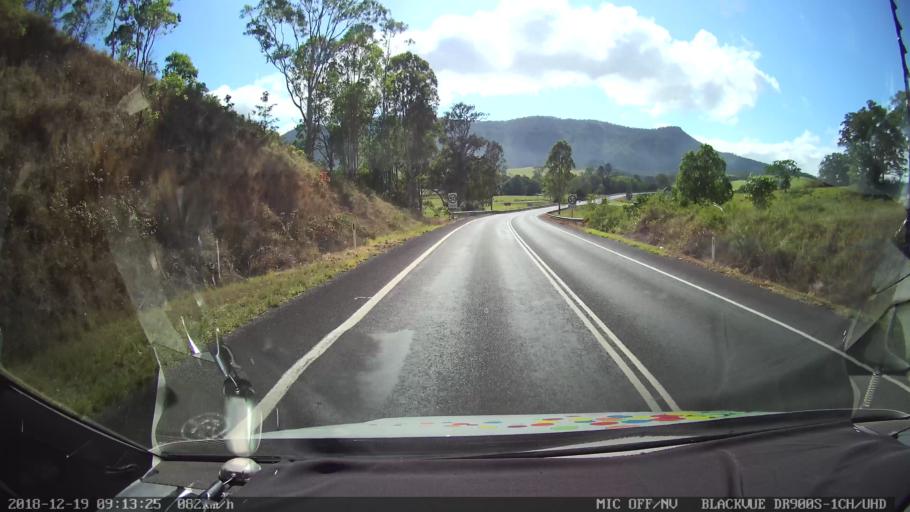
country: AU
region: New South Wales
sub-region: Kyogle
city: Kyogle
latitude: -28.5021
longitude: 152.9625
